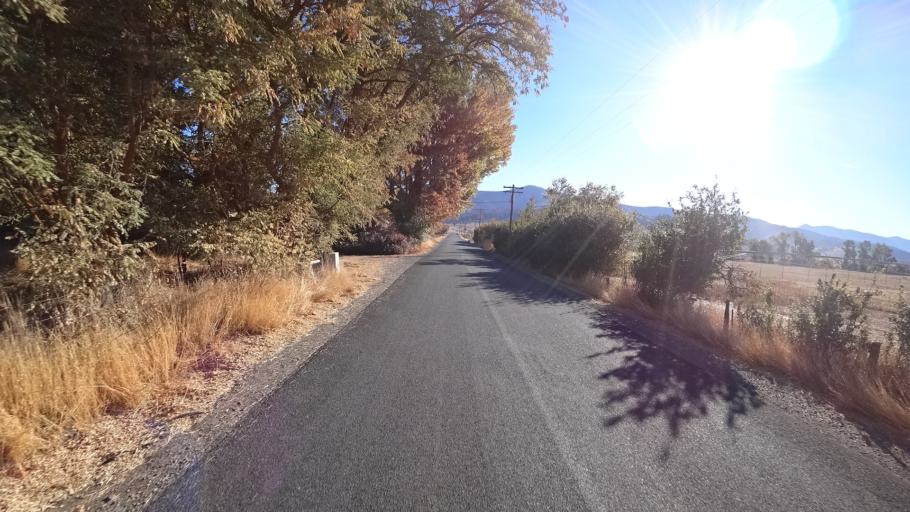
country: US
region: California
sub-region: Siskiyou County
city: Yreka
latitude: 41.4574
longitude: -122.8570
